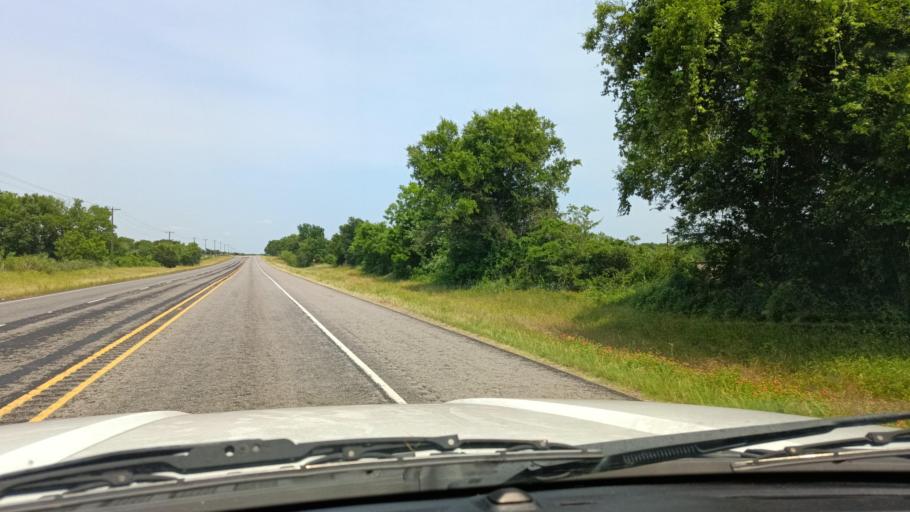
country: US
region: Texas
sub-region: Milam County
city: Cameron
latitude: 30.8488
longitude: -97.0478
